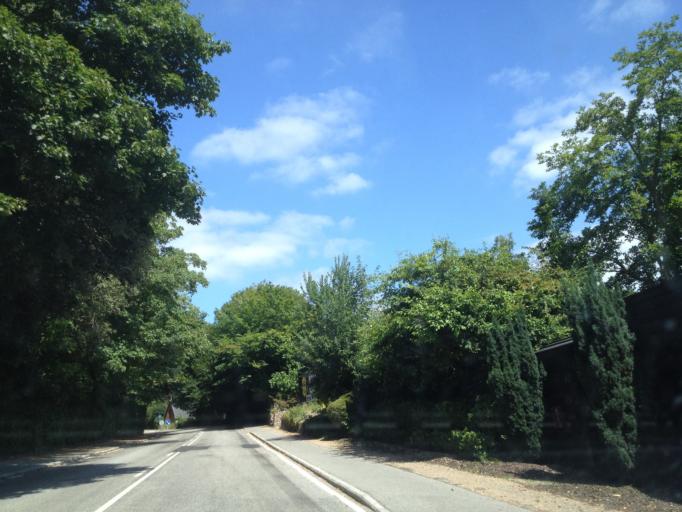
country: DK
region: Capital Region
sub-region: Rudersdal Kommune
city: Trorod
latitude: 55.8415
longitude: 12.5483
